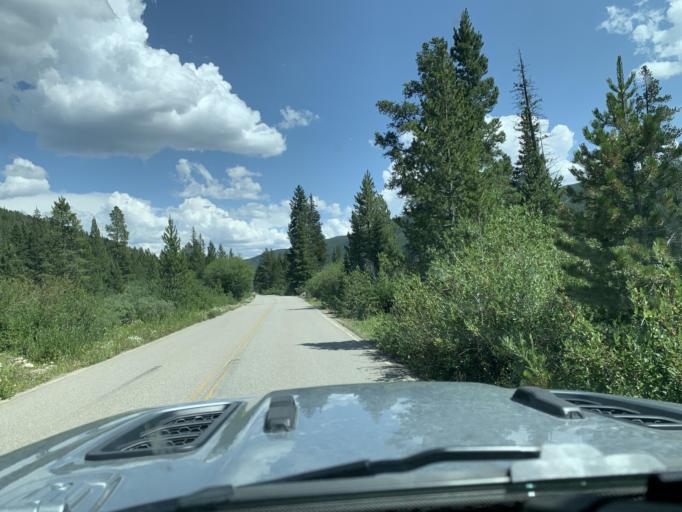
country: US
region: Colorado
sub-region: Lake County
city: Leadville North
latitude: 39.2805
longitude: -106.4388
